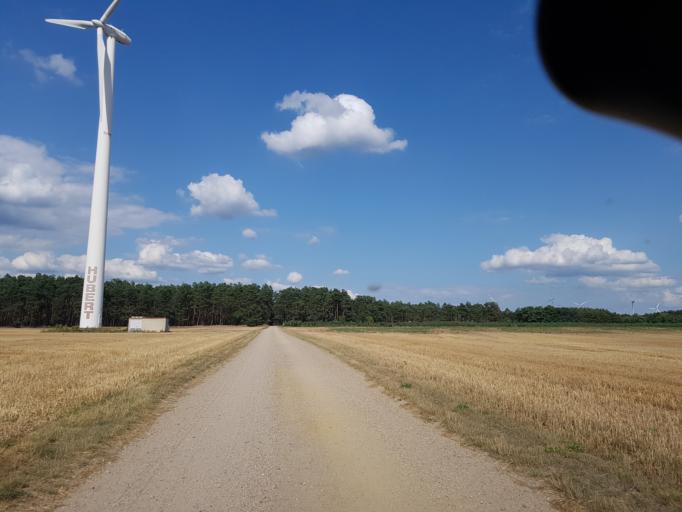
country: DE
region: Brandenburg
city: Finsterwalde
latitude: 51.6358
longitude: 13.7709
